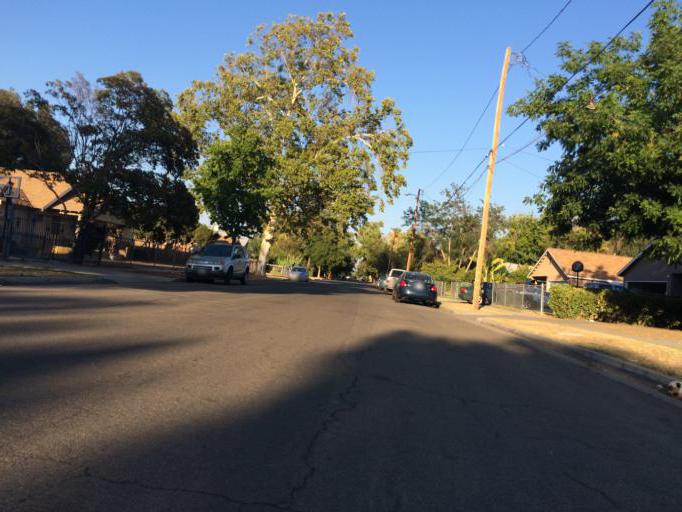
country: US
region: California
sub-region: Fresno County
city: Fresno
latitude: 36.7477
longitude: -119.7408
